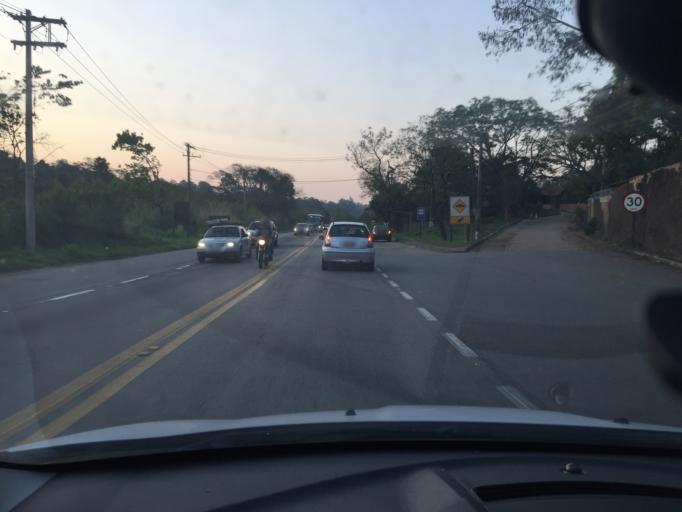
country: BR
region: Sao Paulo
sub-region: Varzea Paulista
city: Varzea Paulista
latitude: -23.2396
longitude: -46.8556
